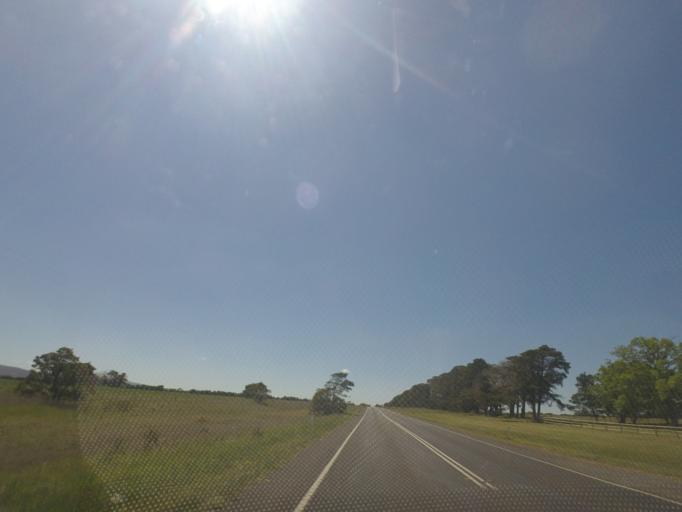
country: AU
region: Victoria
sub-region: Hume
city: Sunbury
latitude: -37.4605
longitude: 144.7415
